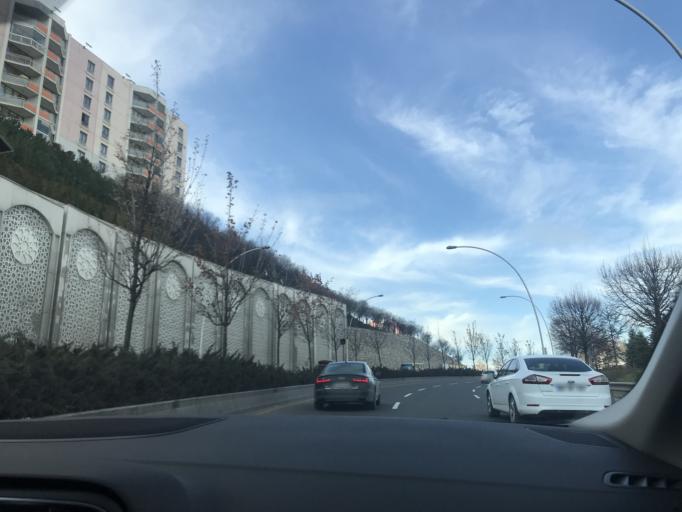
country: TR
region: Ankara
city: Mamak
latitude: 40.0031
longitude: 32.8931
